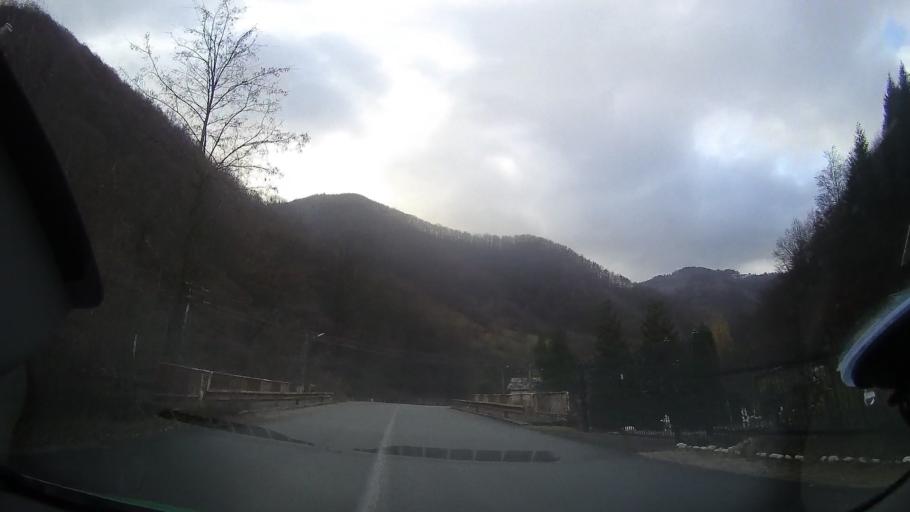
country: RO
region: Cluj
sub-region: Comuna Maguri-Racatau
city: Maguri-Racatau
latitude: 46.6716
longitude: 23.2522
